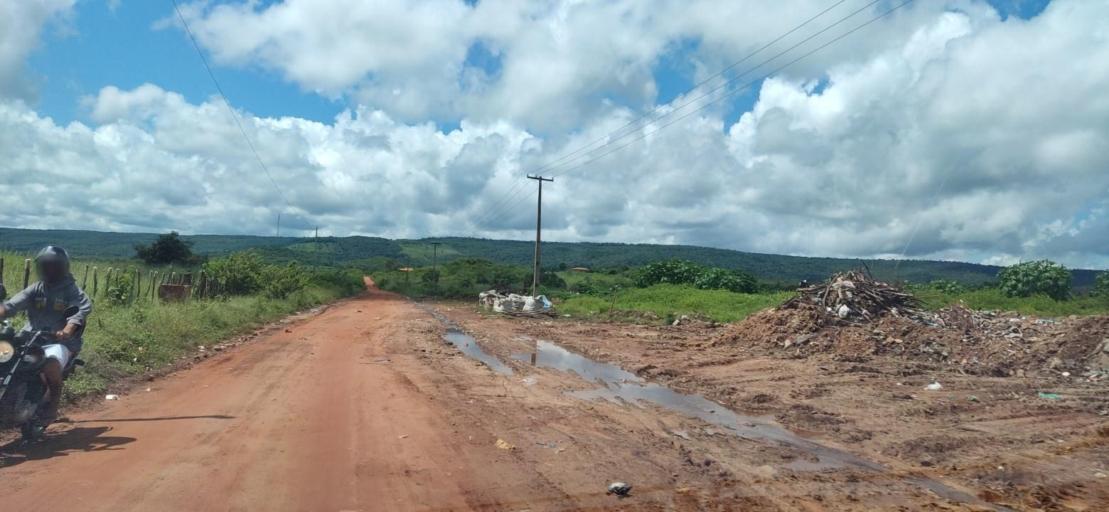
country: BR
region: Piaui
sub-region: Valenca Do Piaui
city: Valenca do Piaui
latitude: -6.1045
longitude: -41.8161
